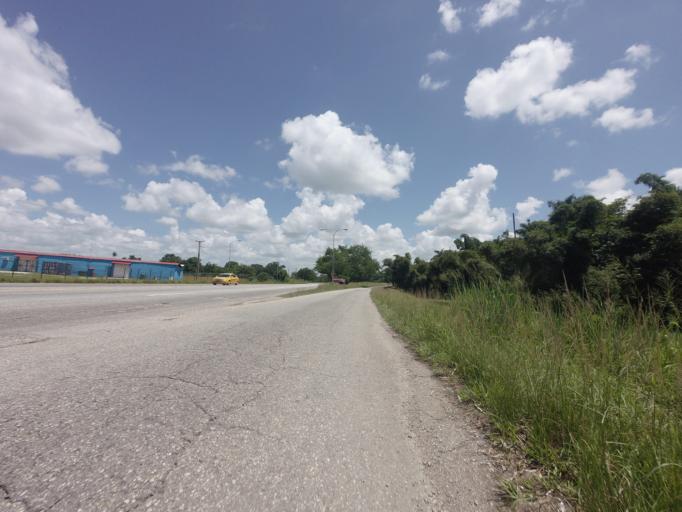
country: CU
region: La Habana
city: Arroyo Naranjo
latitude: 23.0370
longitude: -82.3541
